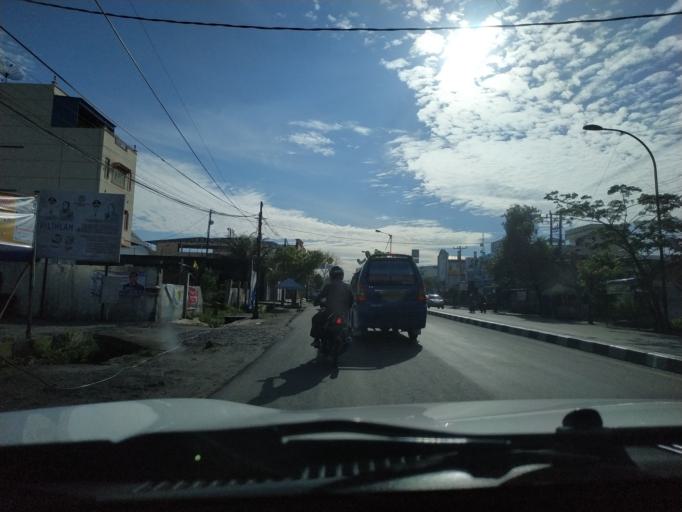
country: ID
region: North Sumatra
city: Medan
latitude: 3.5975
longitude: 98.7207
